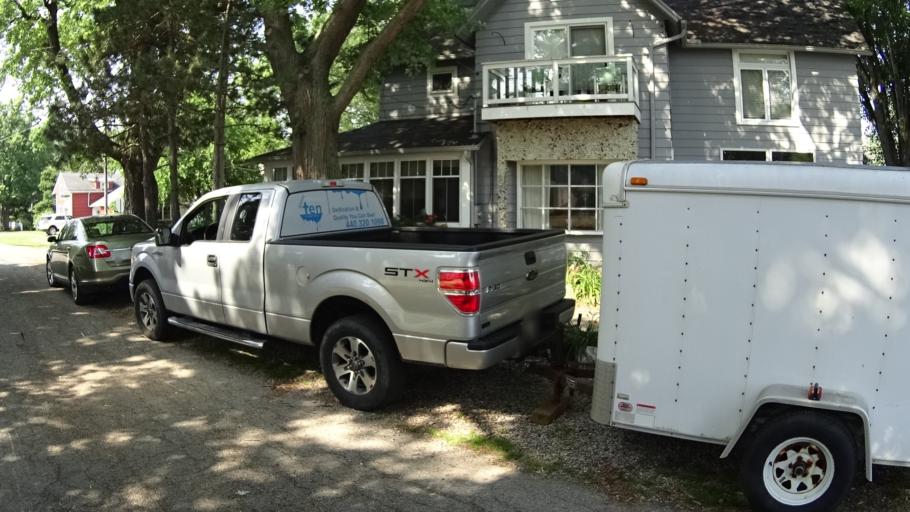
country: US
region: Ohio
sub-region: Lorain County
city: Vermilion
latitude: 41.4246
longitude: -82.3677
